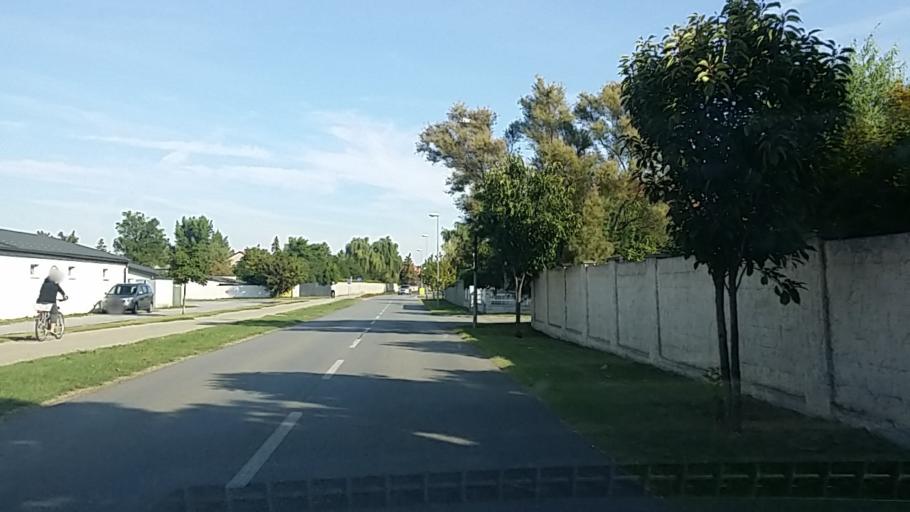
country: AT
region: Burgenland
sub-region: Politischer Bezirk Neusiedl am See
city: Apetlon
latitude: 47.7389
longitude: 16.8332
